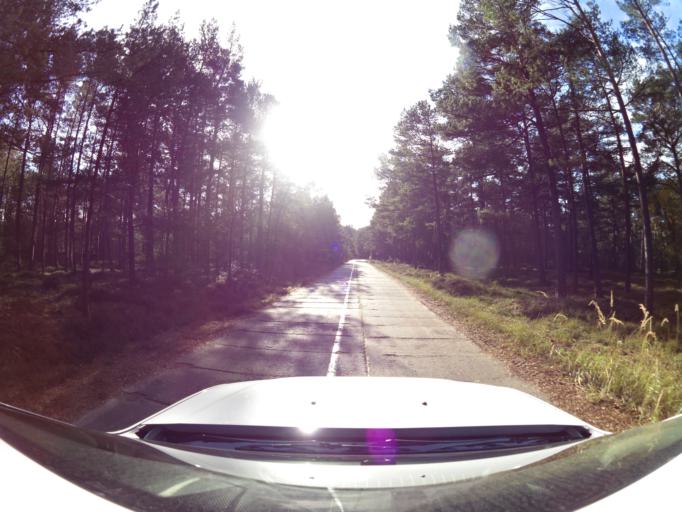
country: PL
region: West Pomeranian Voivodeship
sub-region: Powiat gryficki
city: Cerkwica
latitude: 54.1060
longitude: 15.1484
